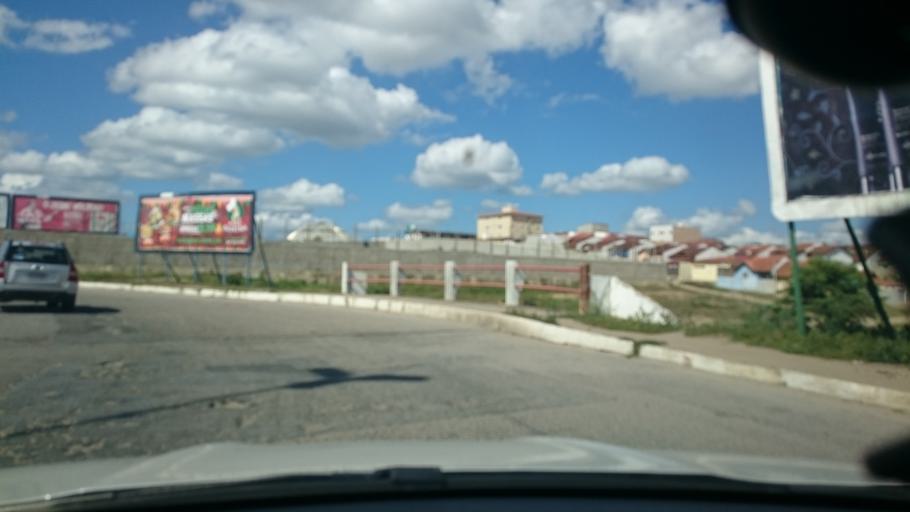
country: BR
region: Paraiba
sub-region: Campina Grande
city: Campina Grande
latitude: -7.2361
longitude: -35.9204
